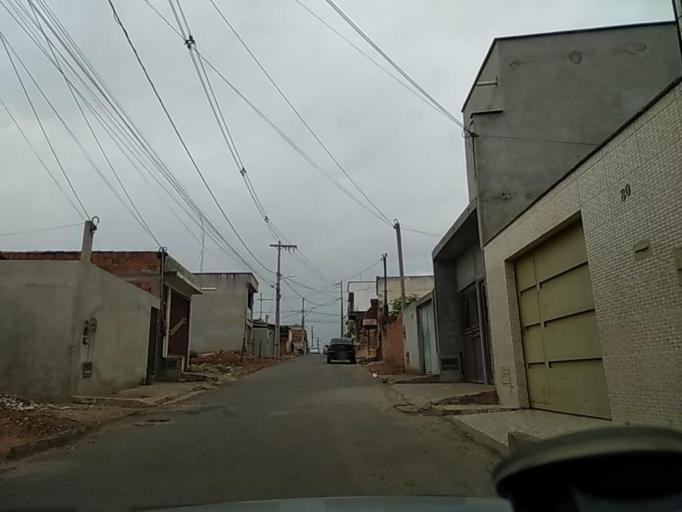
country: BR
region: Bahia
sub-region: Caetite
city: Caetite
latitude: -14.0579
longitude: -42.4799
